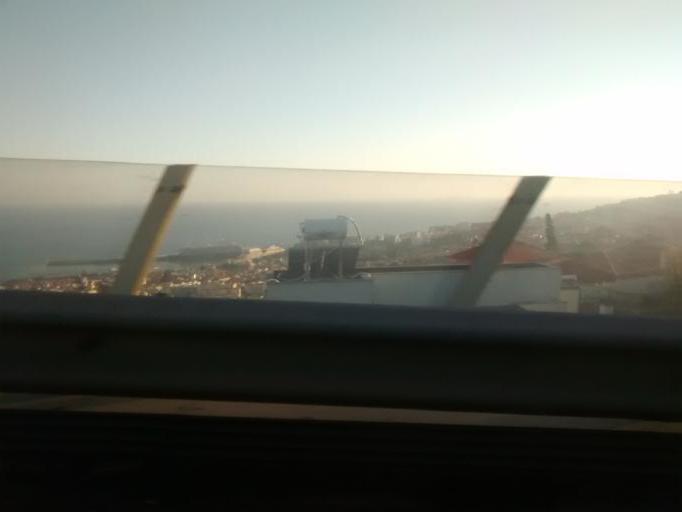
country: PT
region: Madeira
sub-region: Funchal
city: Nossa Senhora do Monte
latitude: 32.6625
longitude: -16.9082
